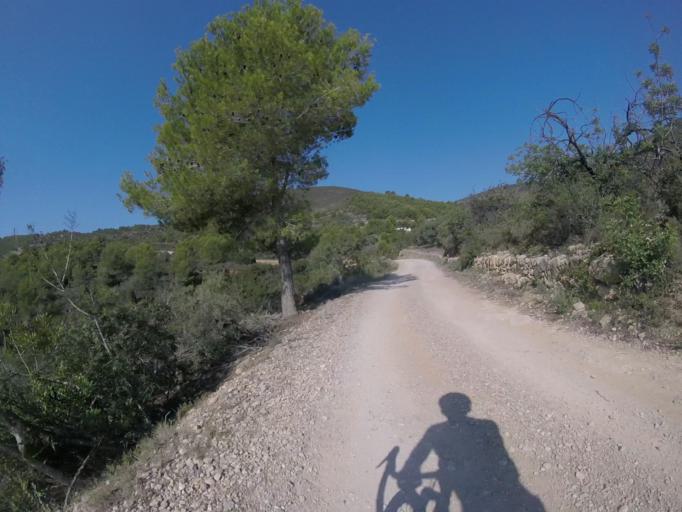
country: ES
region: Valencia
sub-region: Provincia de Castello
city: Peniscola
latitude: 40.3305
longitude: 0.3583
